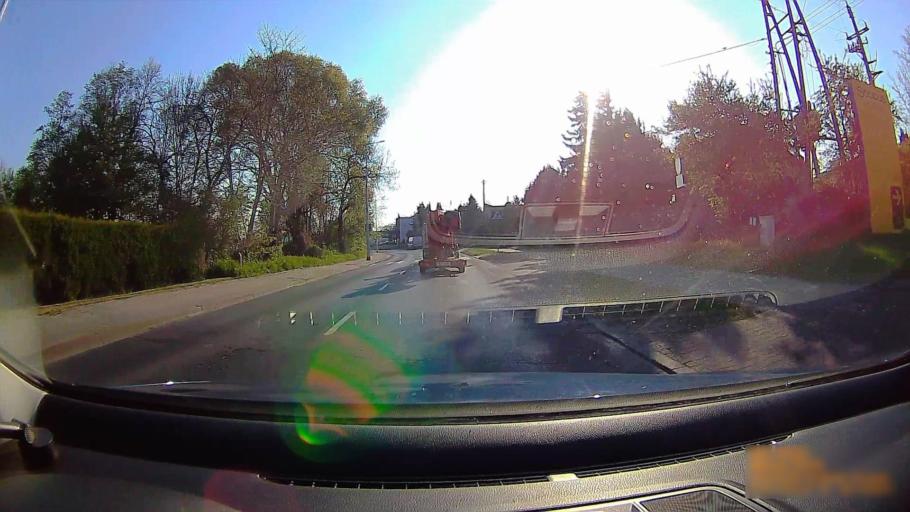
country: PL
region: Greater Poland Voivodeship
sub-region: Konin
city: Konin
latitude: 52.2029
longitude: 18.2407
